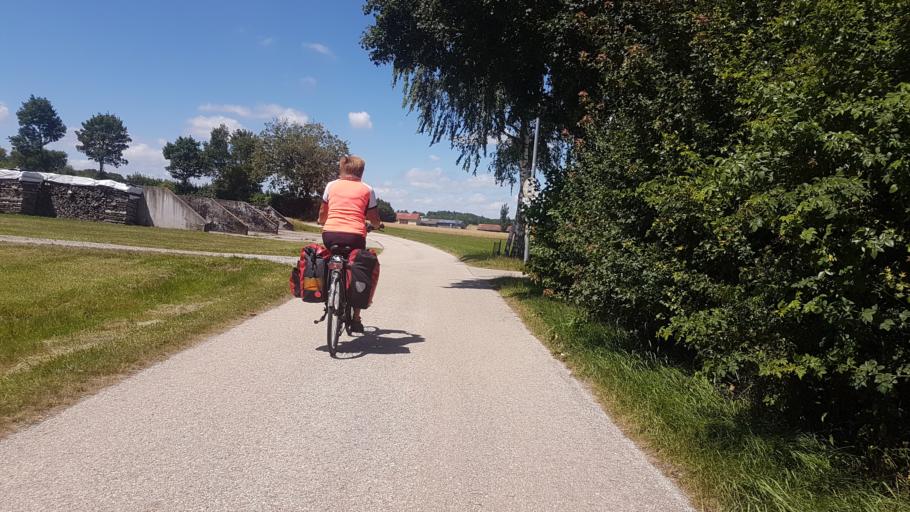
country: DE
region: Bavaria
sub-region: Regierungsbezirk Mittelfranken
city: Leutershausen
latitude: 49.2966
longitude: 10.4054
